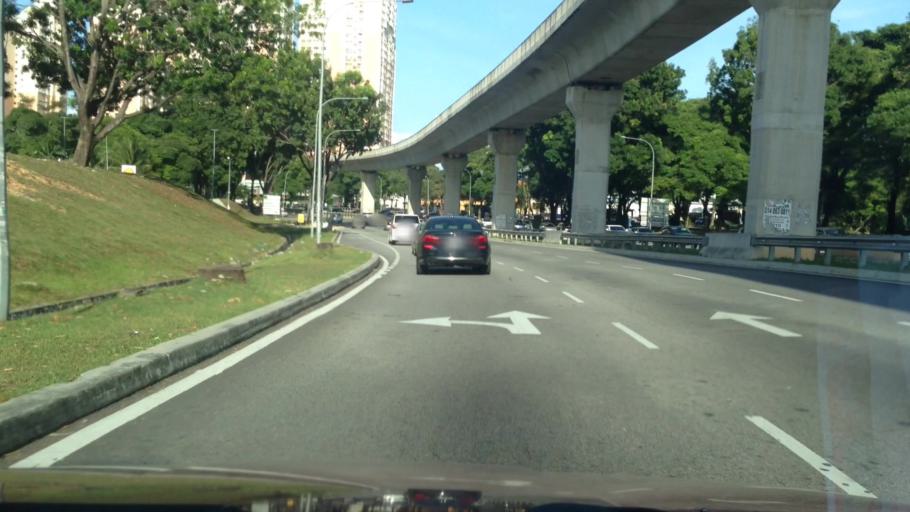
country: MY
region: Selangor
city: Subang Jaya
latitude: 3.0309
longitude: 101.5852
